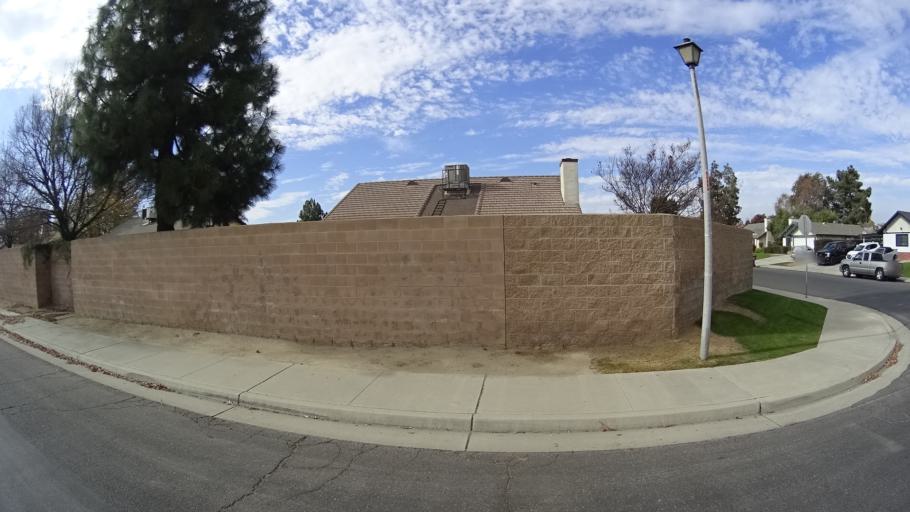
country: US
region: California
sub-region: Kern County
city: Rosedale
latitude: 35.3955
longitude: -119.1367
